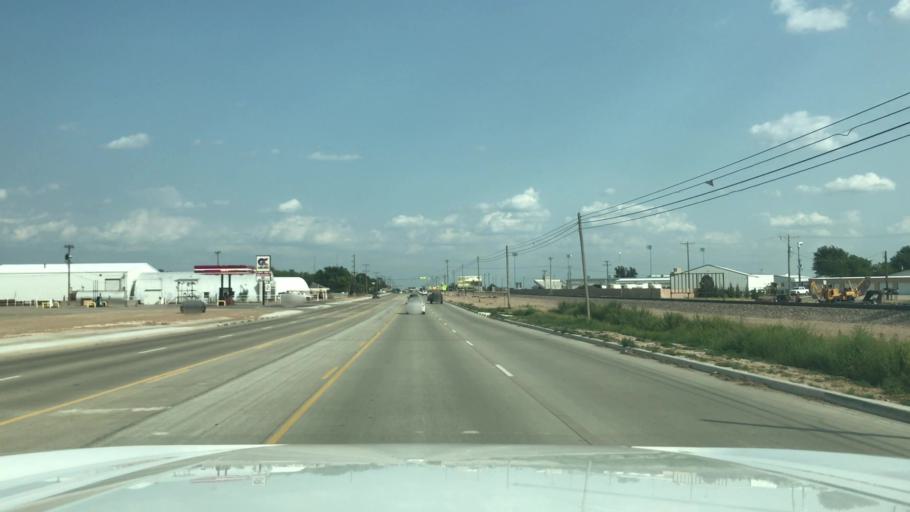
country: US
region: Texas
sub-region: Dallam County
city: Dalhart
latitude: 36.0539
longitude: -102.5051
